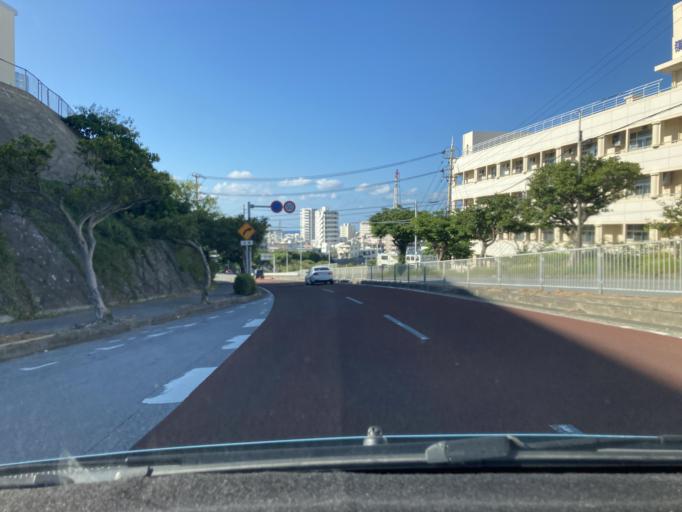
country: JP
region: Okinawa
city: Ginowan
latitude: 26.2595
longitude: 127.7277
